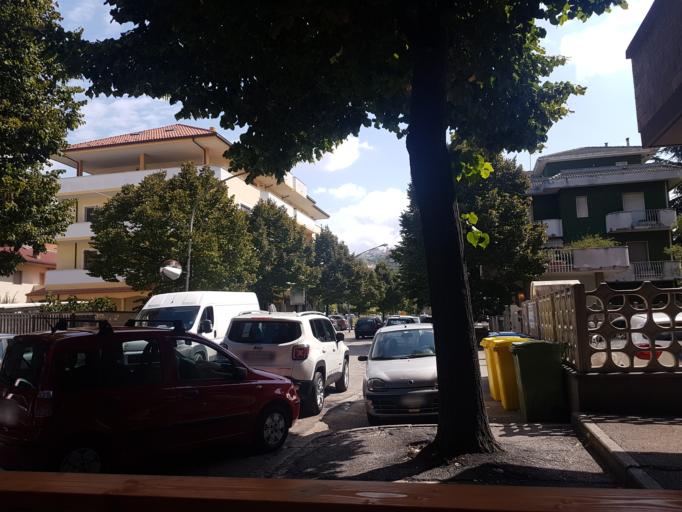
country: IT
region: Abruzzo
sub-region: Provincia di Chieti
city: Chieti
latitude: 42.3497
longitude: 14.1375
